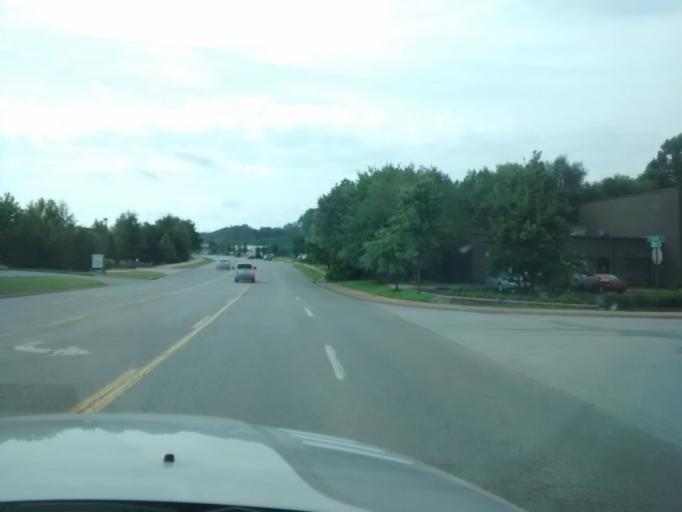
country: US
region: Arkansas
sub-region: Washington County
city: Johnson
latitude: 36.1232
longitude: -94.1427
